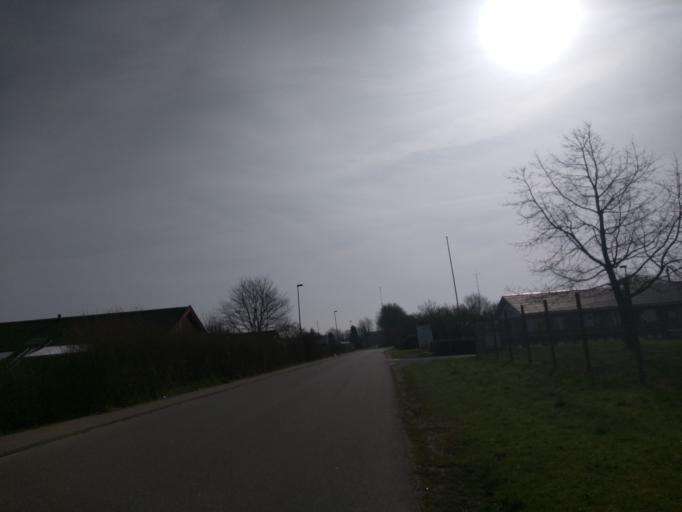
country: DK
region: South Denmark
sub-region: Fredericia Kommune
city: Snoghoj
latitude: 55.5453
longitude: 9.7016
